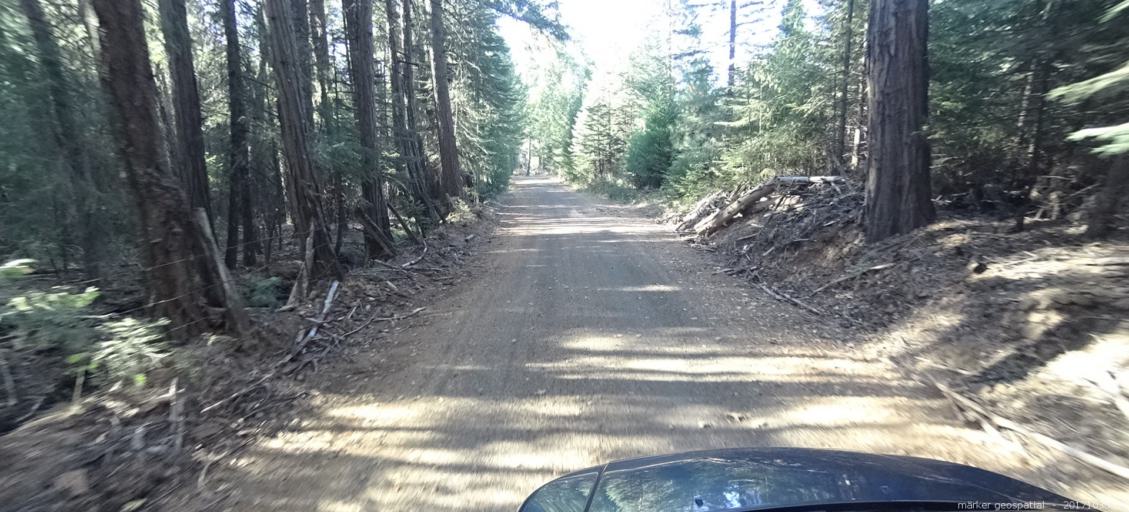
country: US
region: California
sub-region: Shasta County
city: Shingletown
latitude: 40.5329
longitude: -121.7131
